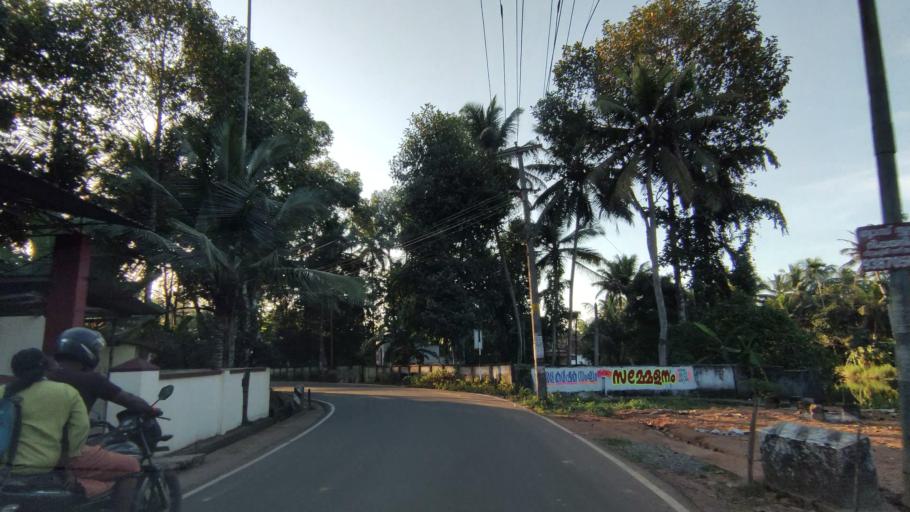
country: IN
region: Kerala
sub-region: Kottayam
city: Kottayam
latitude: 9.6262
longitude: 76.4912
